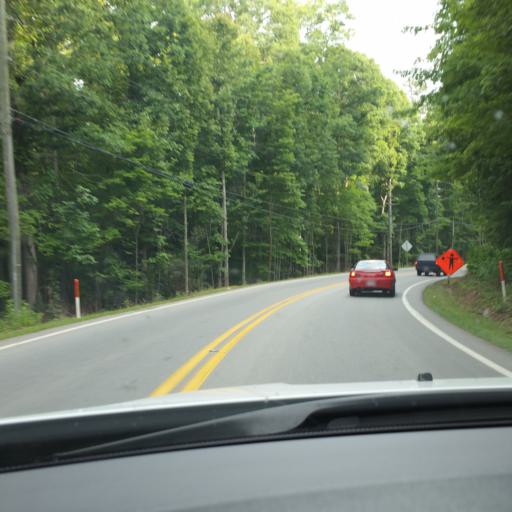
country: US
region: North Carolina
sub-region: Buncombe County
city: Bent Creek
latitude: 35.5353
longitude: -82.6601
